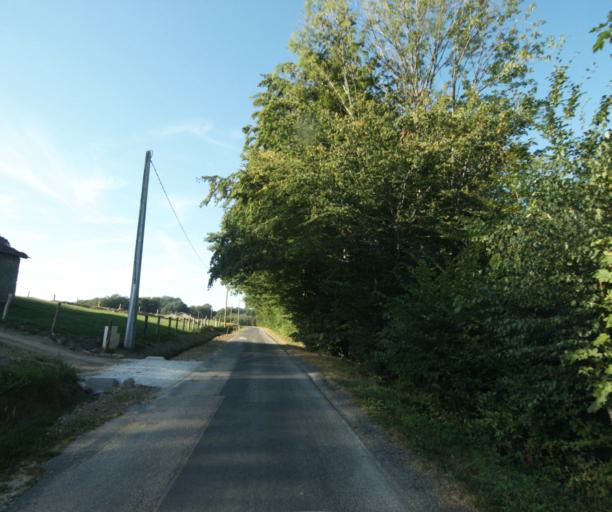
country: FR
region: Lorraine
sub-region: Departement des Vosges
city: Urimenil
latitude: 48.1374
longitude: 6.3945
